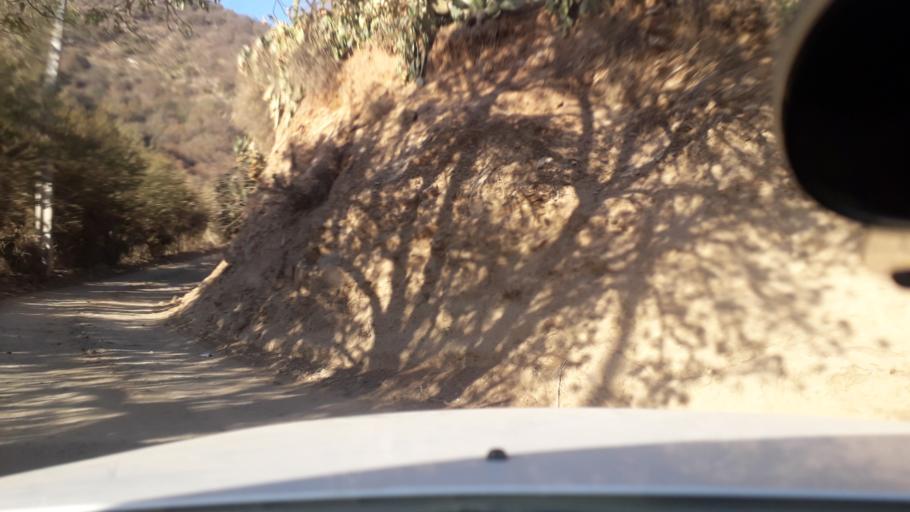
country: CL
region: Valparaiso
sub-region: Provincia de Marga Marga
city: Limache
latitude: -33.0519
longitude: -71.0768
